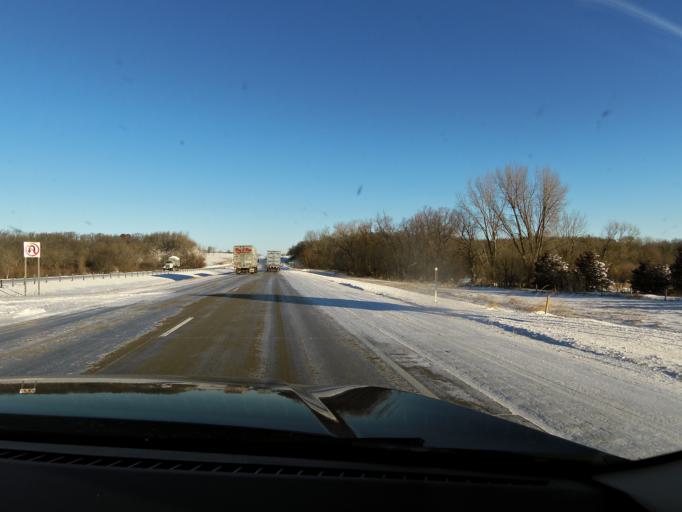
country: US
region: Minnesota
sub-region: Steele County
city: Owatonna
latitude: 43.9823
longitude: -93.2550
